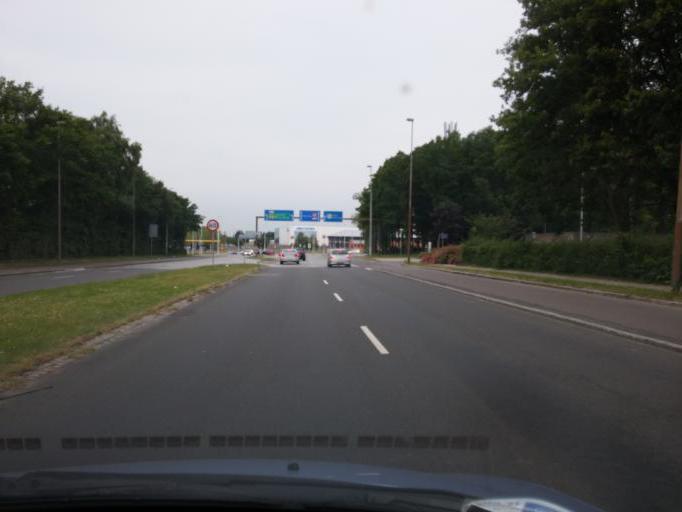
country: DK
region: South Denmark
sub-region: Odense Kommune
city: Seden
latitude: 55.4020
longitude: 10.4282
